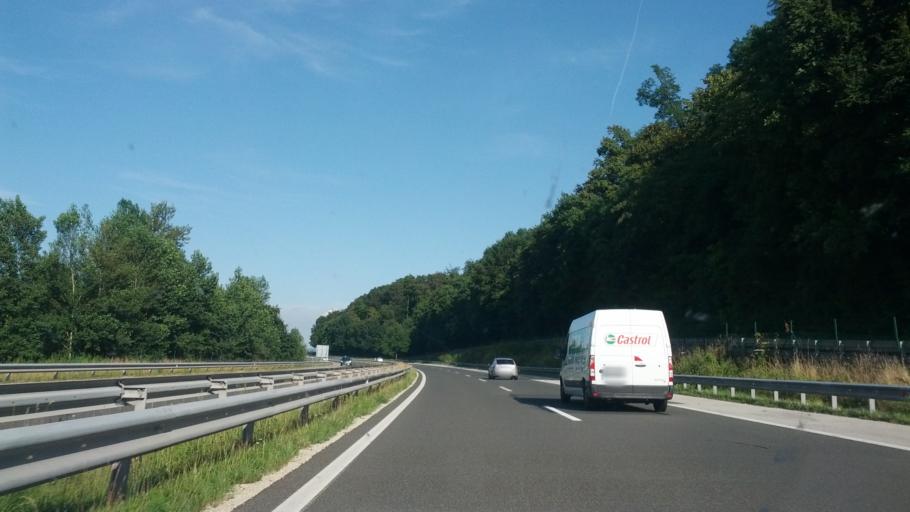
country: SI
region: Brezice
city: Brezice
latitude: 45.8789
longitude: 15.6289
